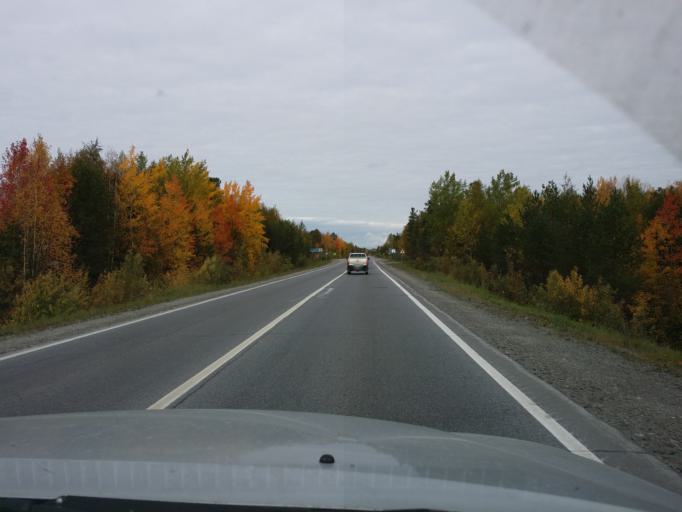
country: RU
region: Khanty-Mansiyskiy Avtonomnyy Okrug
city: Megion
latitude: 61.1043
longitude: 75.8531
